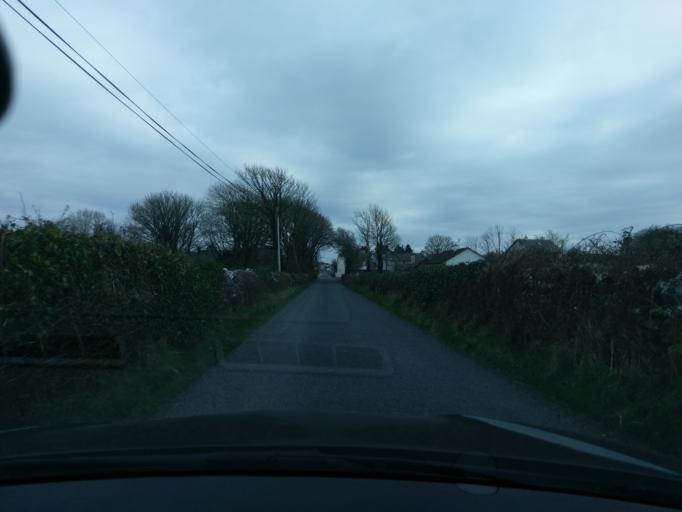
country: IE
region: Connaught
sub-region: County Galway
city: Oranmore
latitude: 53.1873
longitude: -8.9102
